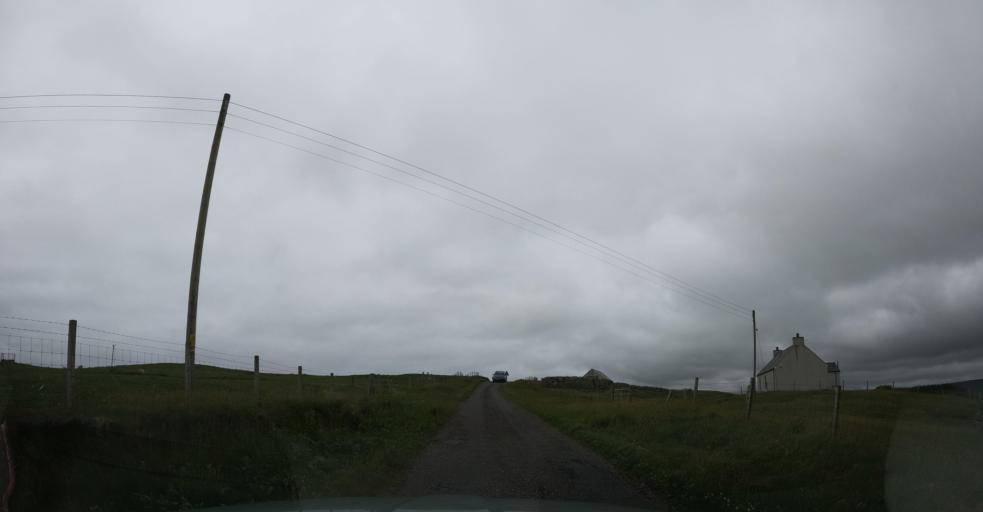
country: GB
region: Scotland
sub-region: Eilean Siar
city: Isle of North Uist
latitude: 57.5368
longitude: -7.3505
